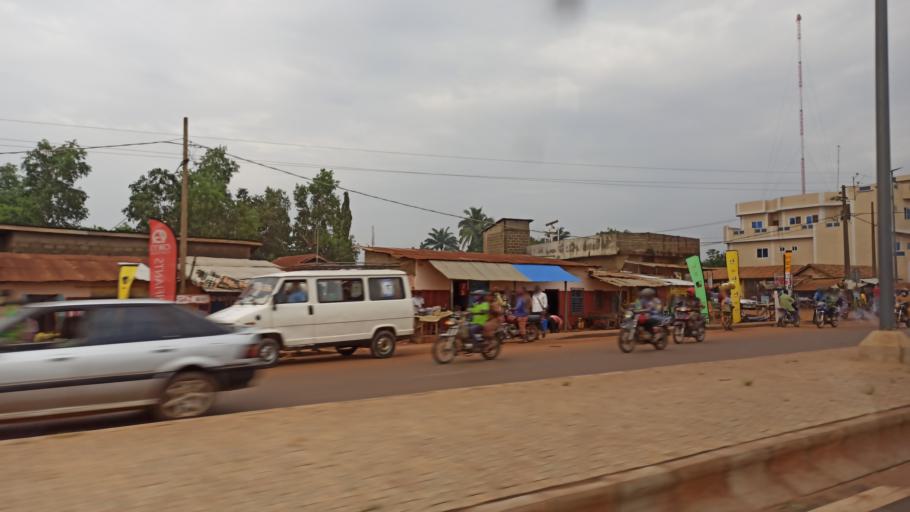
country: BJ
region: Queme
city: Porto-Novo
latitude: 6.5359
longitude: 2.5959
